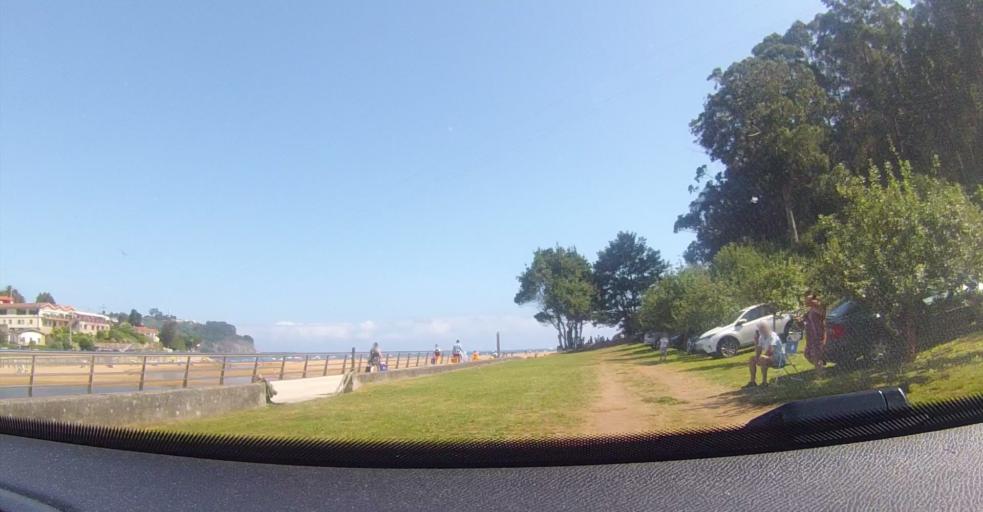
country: ES
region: Asturias
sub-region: Province of Asturias
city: Colunga
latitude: 43.4988
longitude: -5.2618
